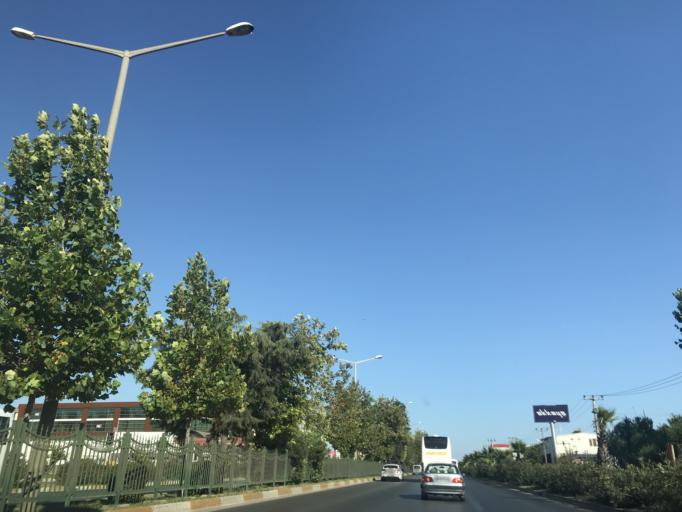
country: TR
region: Antalya
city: Antalya
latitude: 36.9051
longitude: 30.7529
